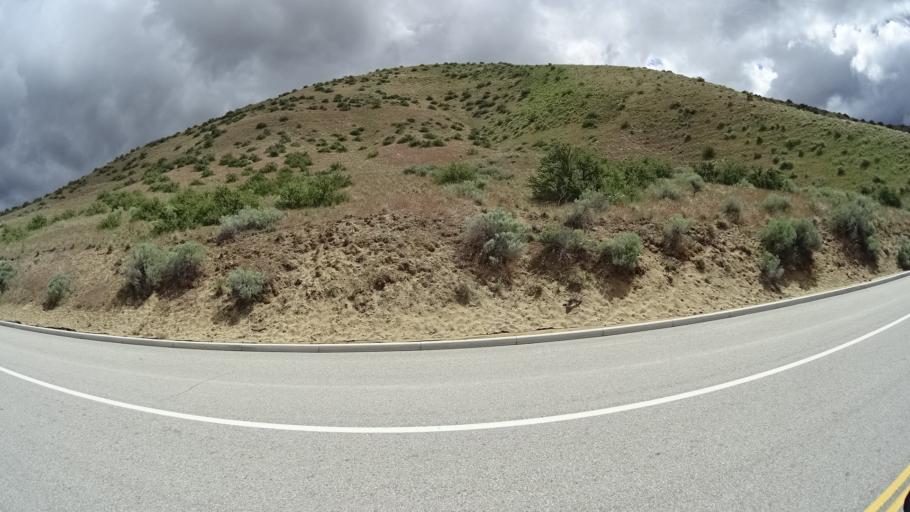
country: US
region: Idaho
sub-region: Ada County
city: Boise
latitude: 43.6845
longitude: -116.1835
